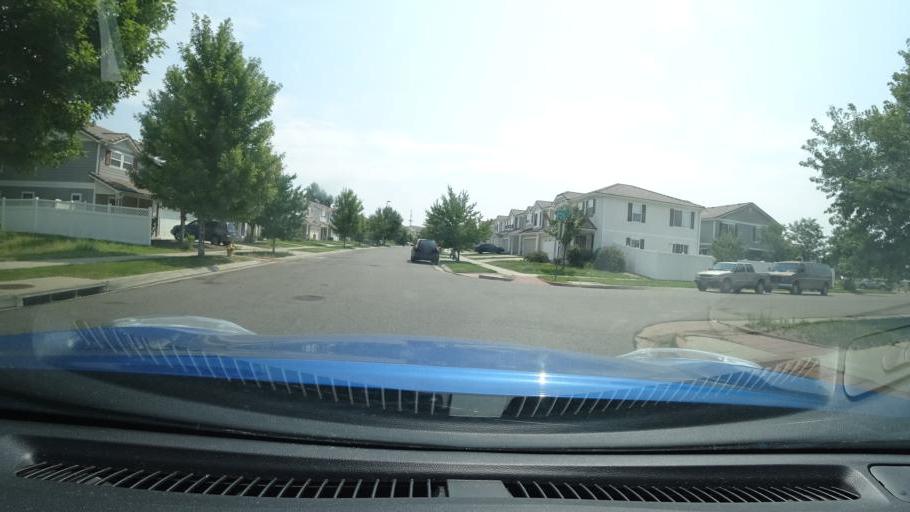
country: US
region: Colorado
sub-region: Adams County
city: Aurora
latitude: 39.7833
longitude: -104.7595
